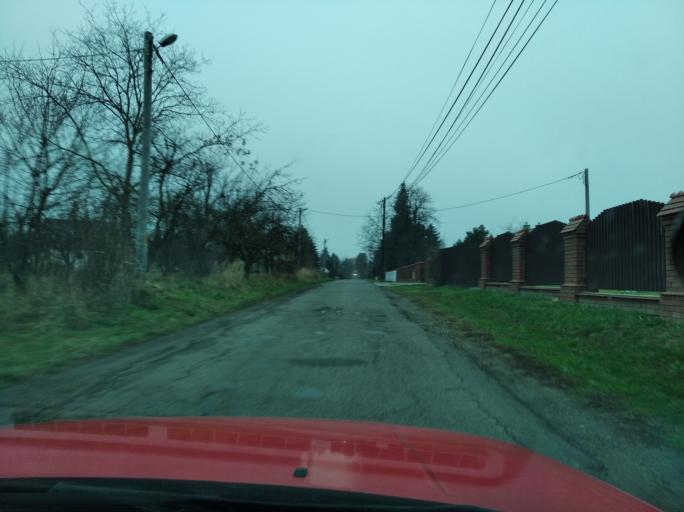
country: PL
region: Subcarpathian Voivodeship
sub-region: Powiat jaroslawski
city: Pawlosiow
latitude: 50.0148
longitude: 22.6429
